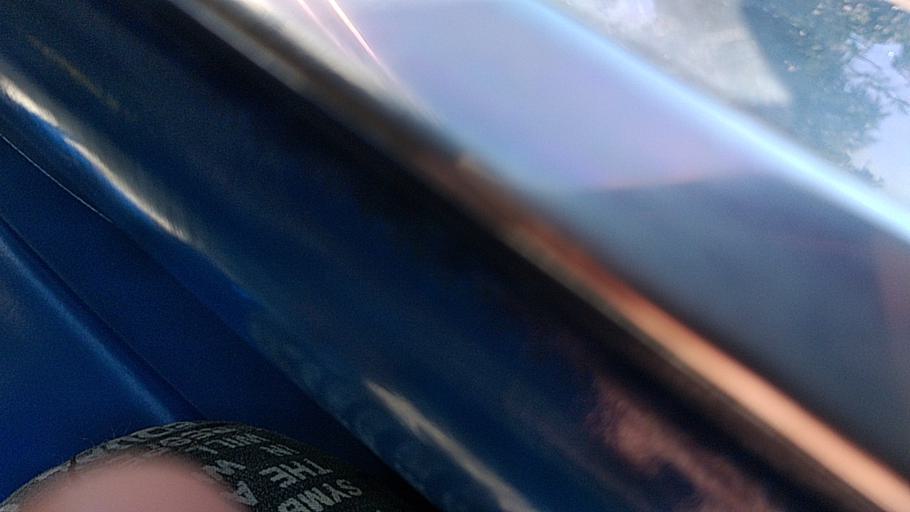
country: TH
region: Nakhon Ratchasima
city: Nakhon Ratchasima
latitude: 14.9767
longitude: 102.0978
